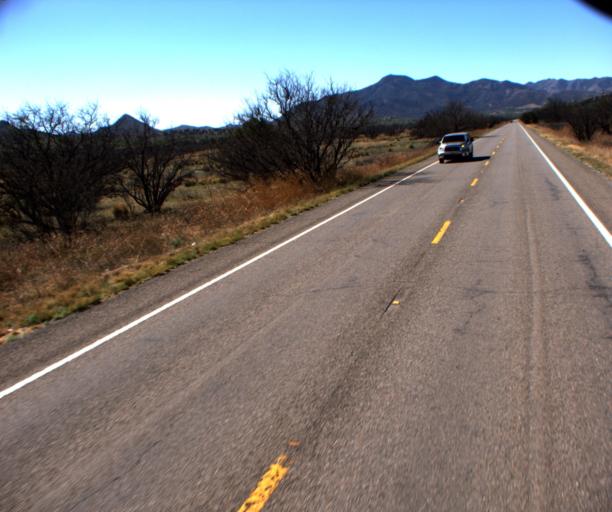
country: US
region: Arizona
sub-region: Santa Cruz County
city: Rio Rico
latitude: 31.5843
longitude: -110.7276
